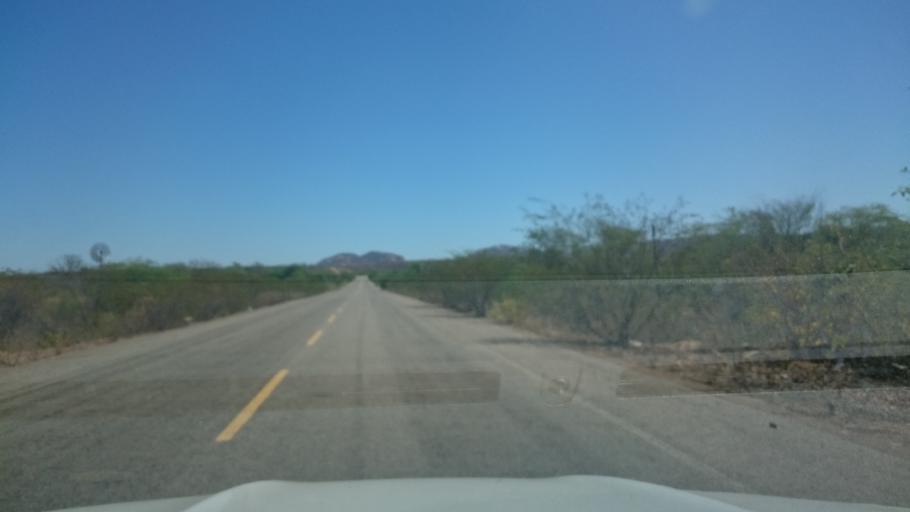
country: BR
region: Rio Grande do Norte
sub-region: Alexandria
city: Alexandria
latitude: -6.1988
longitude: -37.9594
